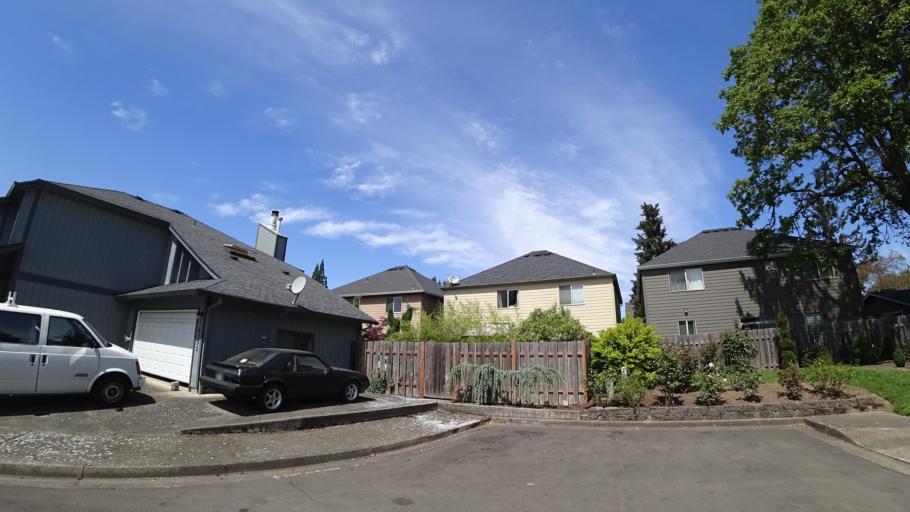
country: US
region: Oregon
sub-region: Washington County
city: Aloha
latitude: 45.4876
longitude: -122.8498
